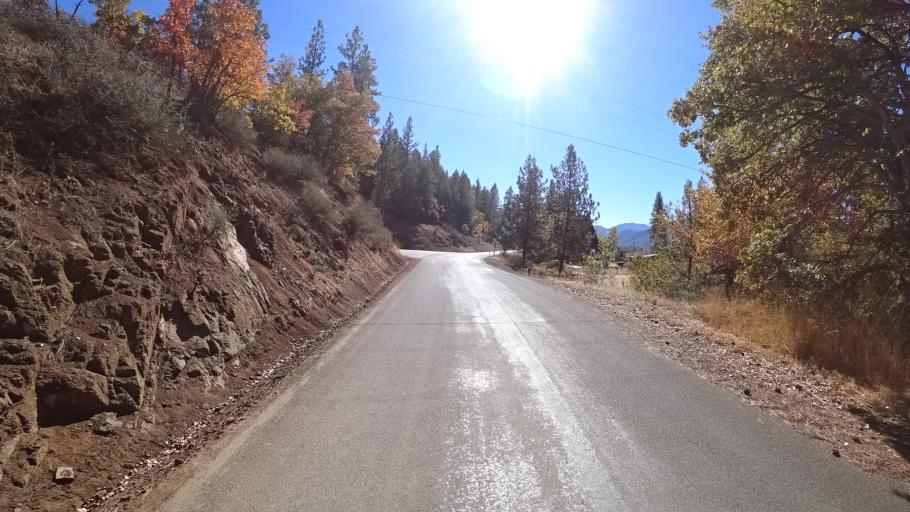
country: US
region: California
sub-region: Siskiyou County
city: Yreka
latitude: 41.6167
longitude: -122.9788
